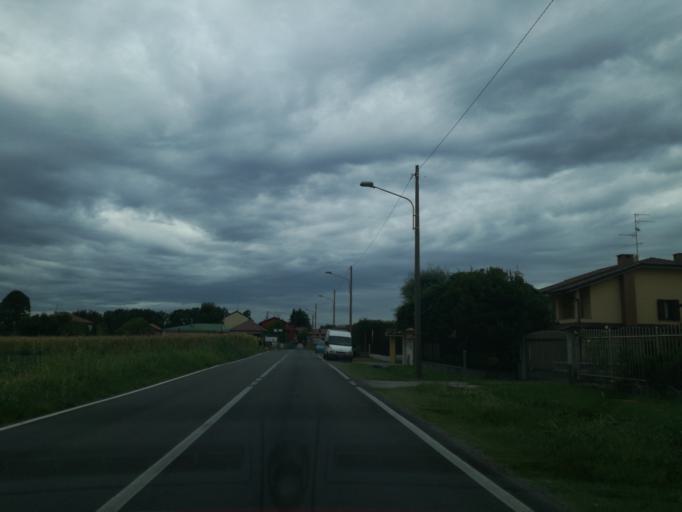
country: IT
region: Lombardy
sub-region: Provincia di Monza e Brianza
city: Sulbiate
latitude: 45.6356
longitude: 9.4367
